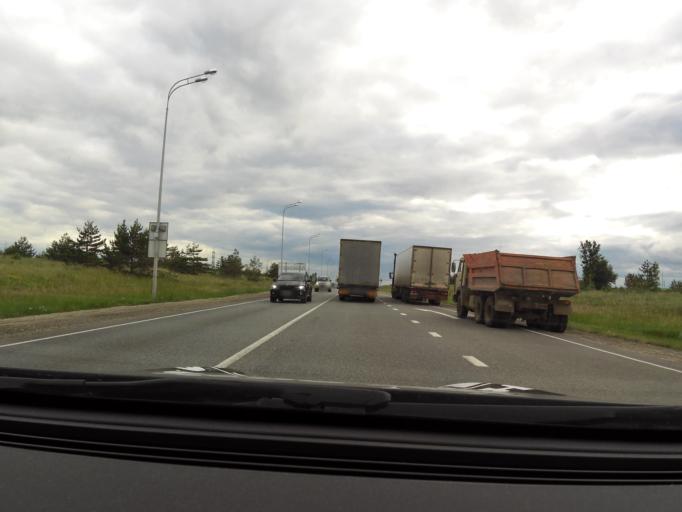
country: RU
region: Tatarstan
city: Sviyazhsk
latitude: 55.7266
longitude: 48.7578
